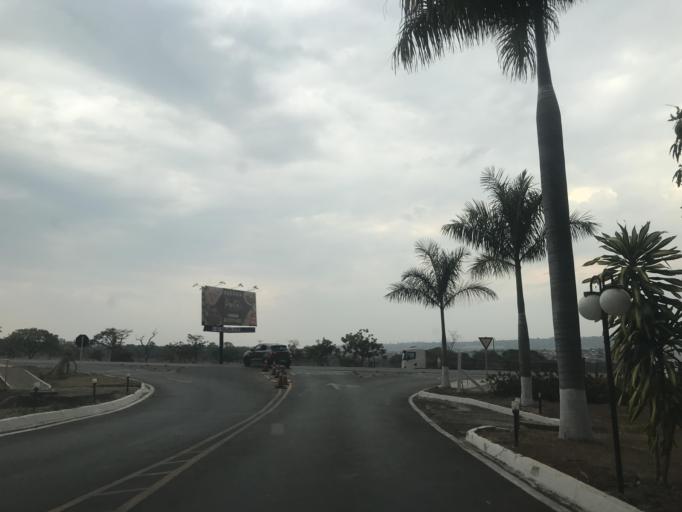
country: BR
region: Federal District
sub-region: Brasilia
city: Brasilia
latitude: -15.6625
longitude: -47.8332
